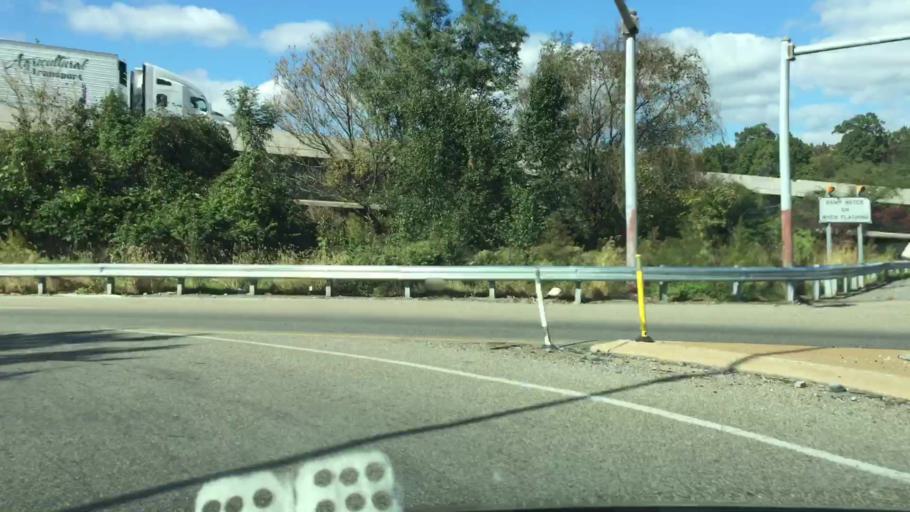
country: US
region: Pennsylvania
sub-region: Delaware County
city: Media
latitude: 39.9375
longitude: -75.3630
